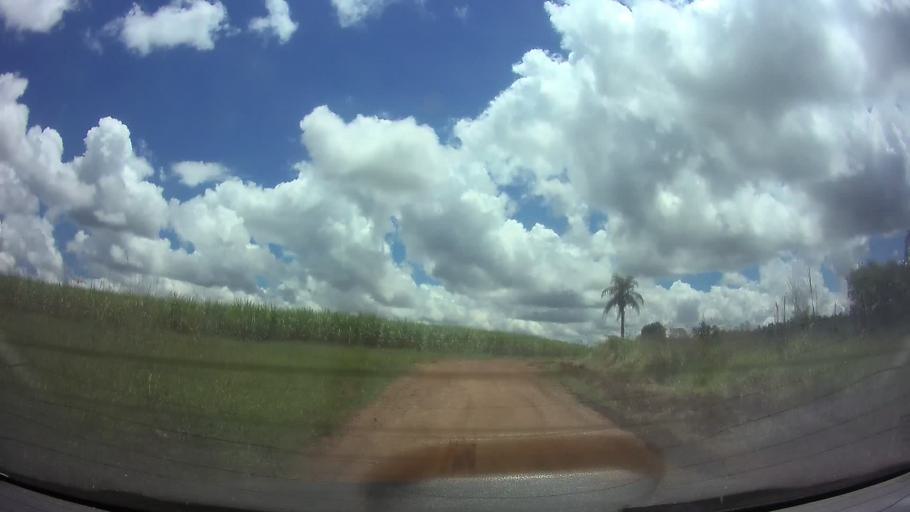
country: PY
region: Paraguari
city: La Colmena
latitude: -25.9659
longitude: -56.7539
